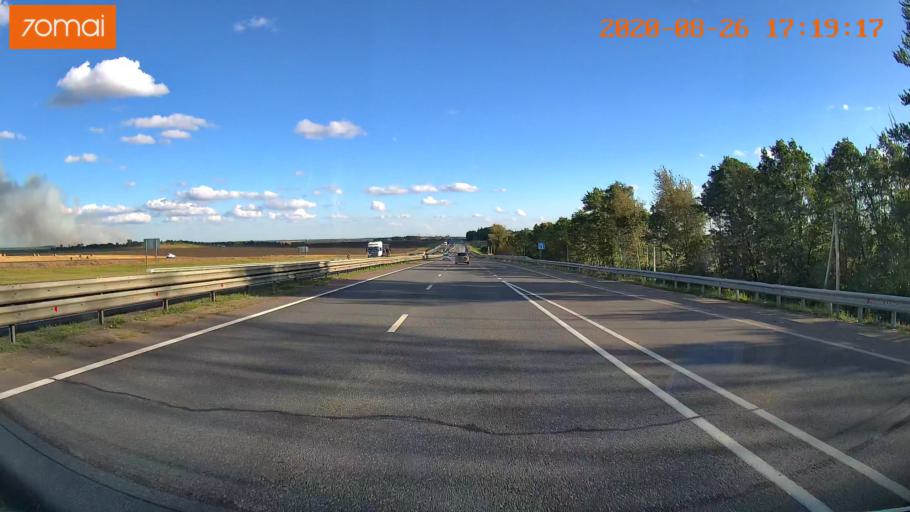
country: RU
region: Tula
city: Volovo
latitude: 53.5971
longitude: 38.1032
